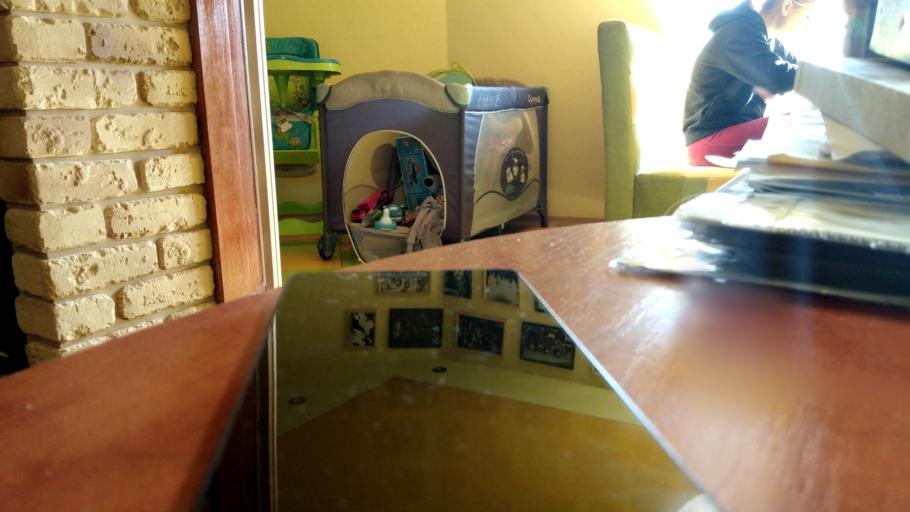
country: RU
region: Penza
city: Serdobsk
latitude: 52.4810
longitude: 44.2705
